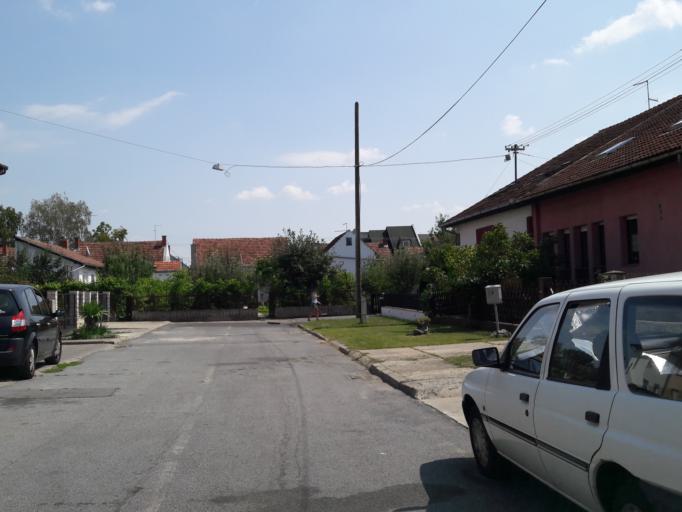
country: HR
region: Osjecko-Baranjska
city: Visnjevac
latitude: 45.5577
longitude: 18.6465
